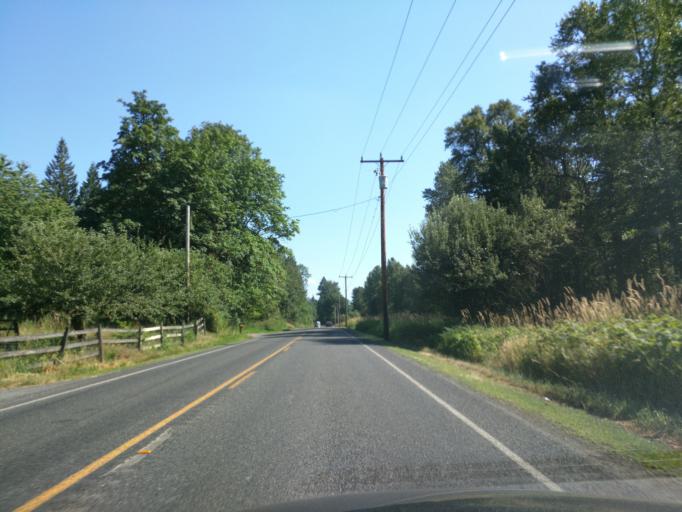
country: US
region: Washington
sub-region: Whatcom County
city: Peaceful Valley
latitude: 48.8049
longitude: -122.1974
